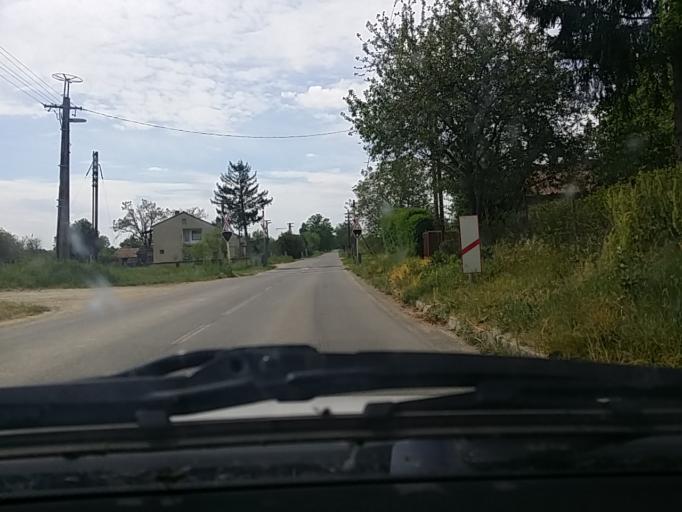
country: HU
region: Somogy
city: Babocsa
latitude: 46.0367
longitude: 17.3370
